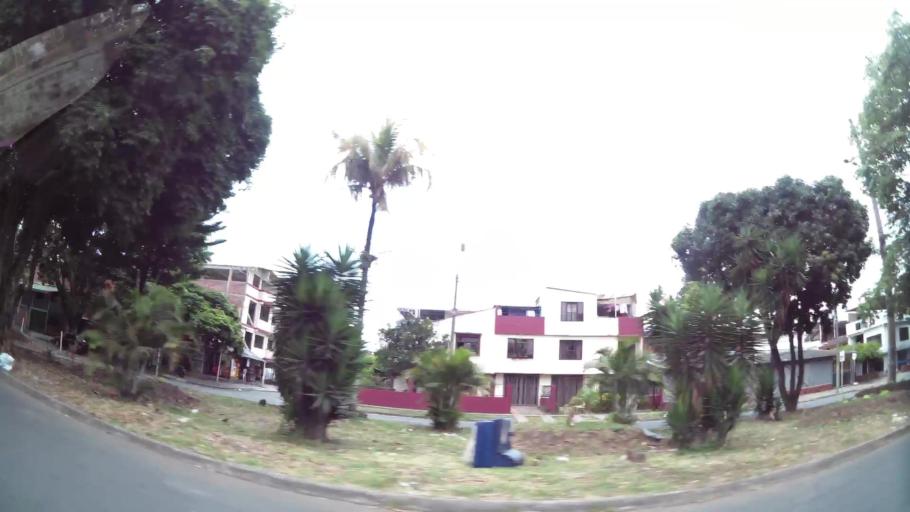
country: CO
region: Valle del Cauca
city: Cali
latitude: 3.4675
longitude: -76.4946
